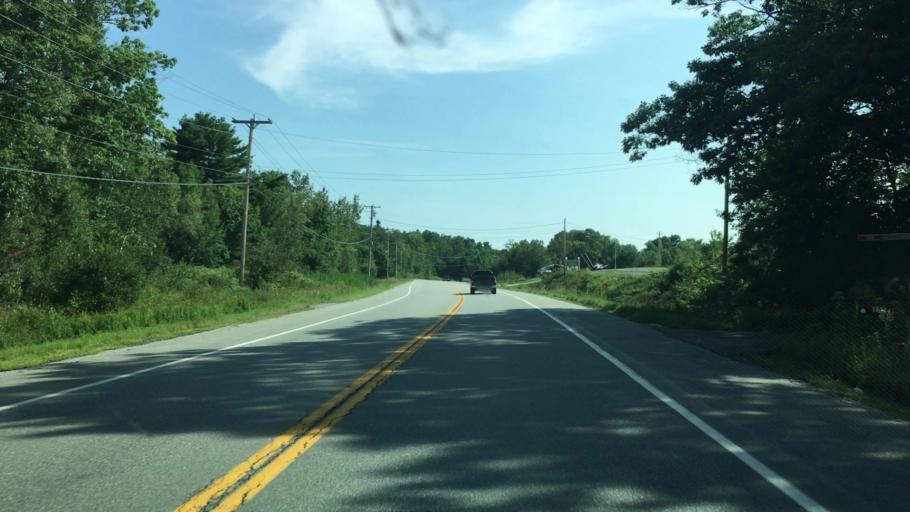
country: US
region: Maine
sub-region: Waldo County
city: Frankfort
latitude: 44.6167
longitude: -68.8698
